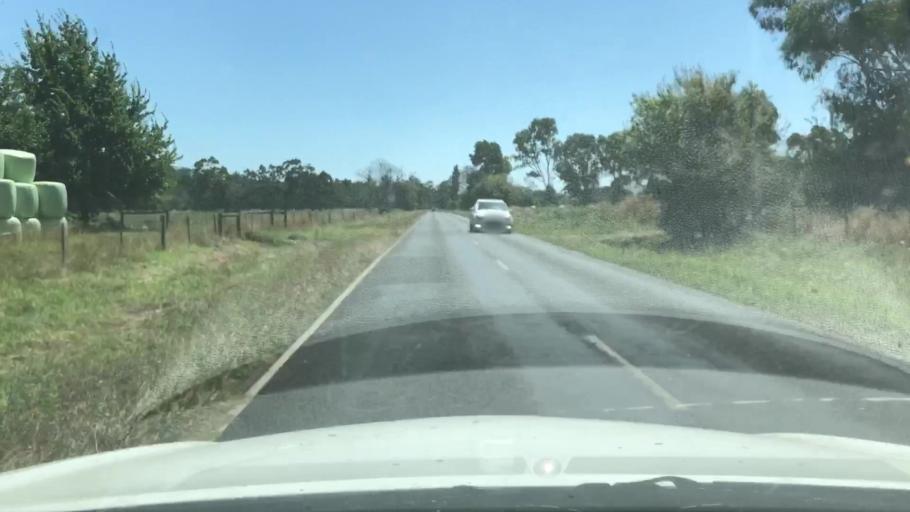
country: AU
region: Victoria
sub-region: Yarra Ranges
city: Yarra Junction
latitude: -37.7757
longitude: 145.6141
